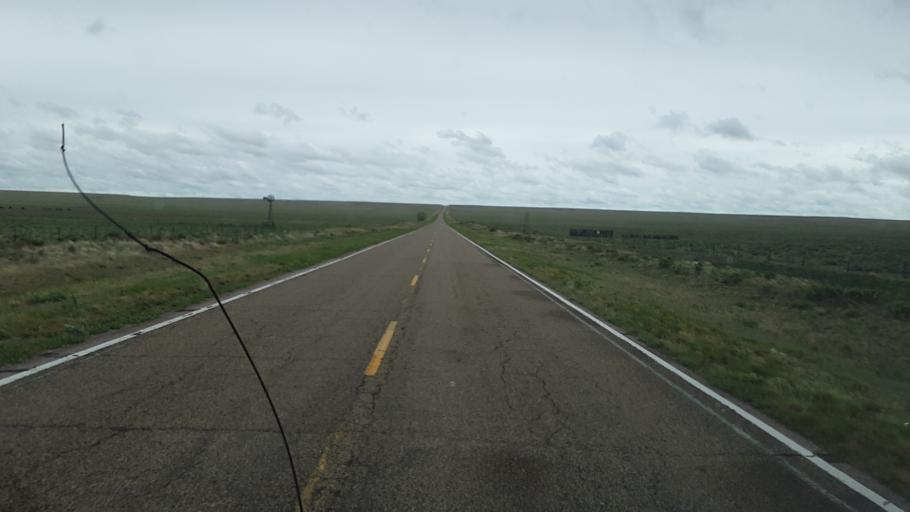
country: US
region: Colorado
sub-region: Lincoln County
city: Hugo
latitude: 38.8498
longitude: -103.3638
